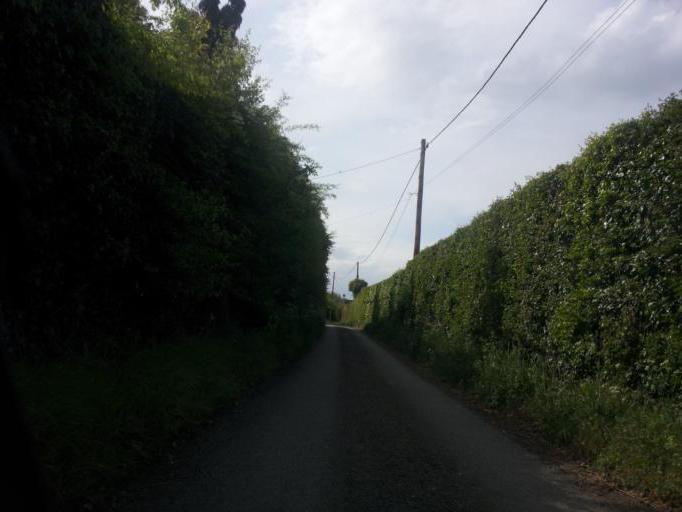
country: GB
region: England
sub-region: Kent
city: Teynham
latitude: 51.3293
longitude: 0.8443
